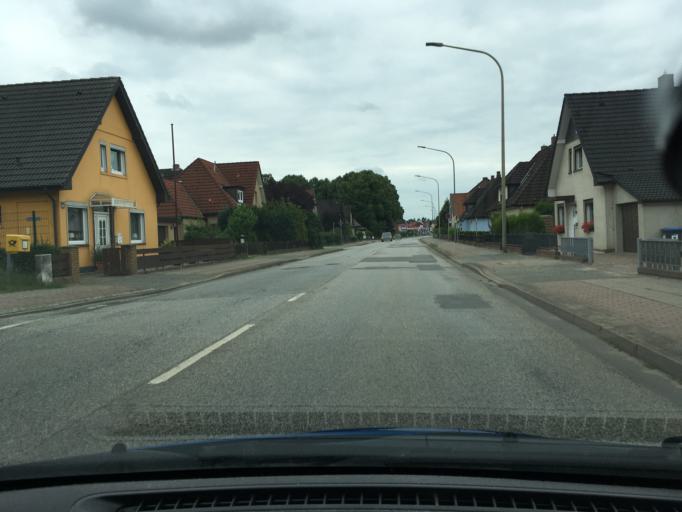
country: DE
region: Schleswig-Holstein
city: Geesthacht
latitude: 53.4475
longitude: 10.3610
